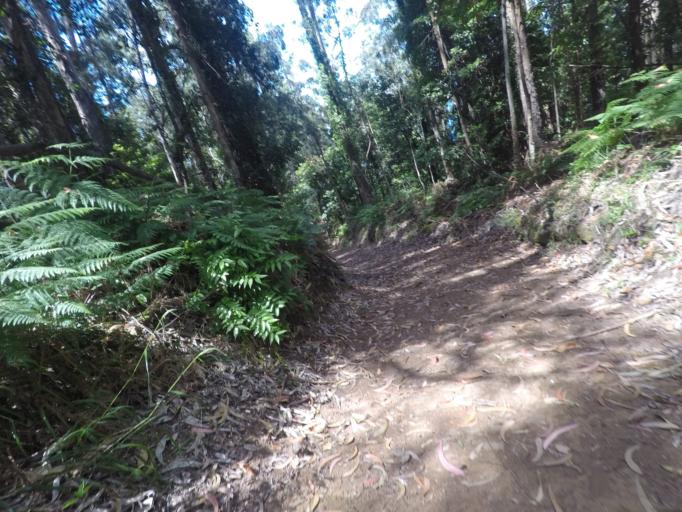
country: PT
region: Madeira
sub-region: Porto Moniz
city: Porto Moniz
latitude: 32.8417
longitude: -17.1487
